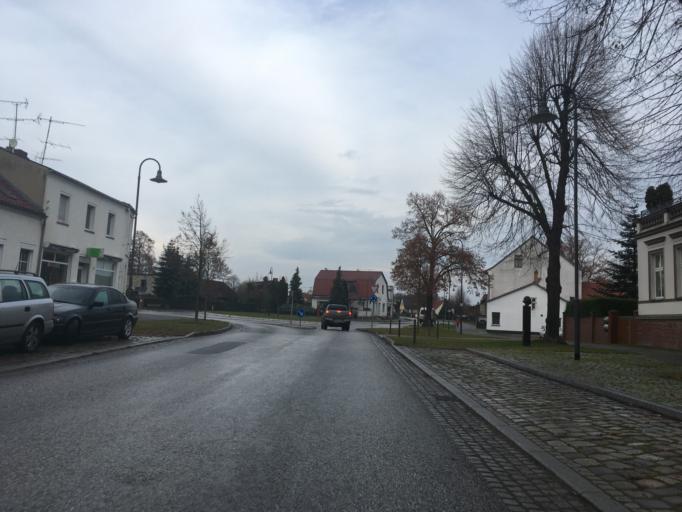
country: DE
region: Brandenburg
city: Letschin
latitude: 52.6462
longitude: 14.3599
